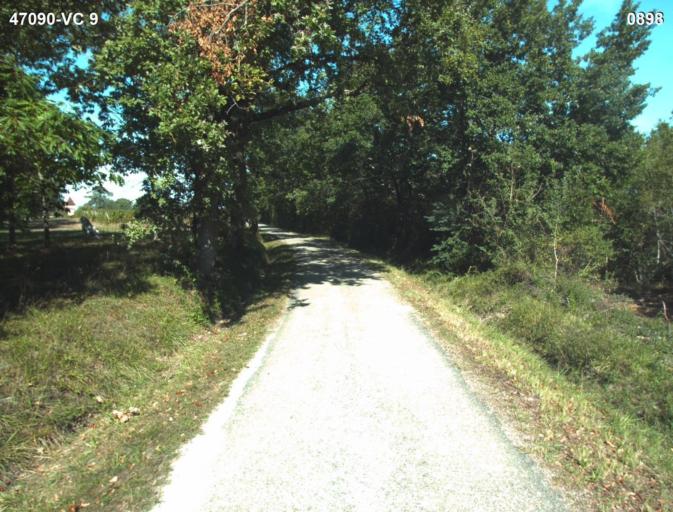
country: FR
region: Aquitaine
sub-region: Departement du Lot-et-Garonne
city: Nerac
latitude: 44.1792
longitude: 0.3875
